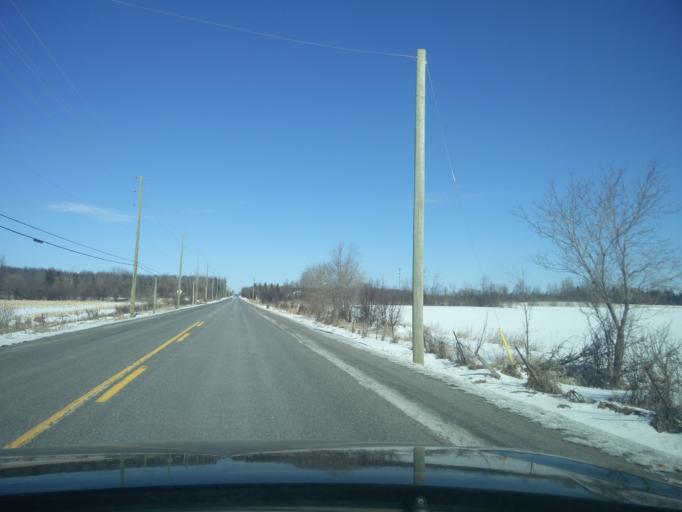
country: CA
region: Ontario
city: Bells Corners
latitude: 45.2269
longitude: -75.7207
